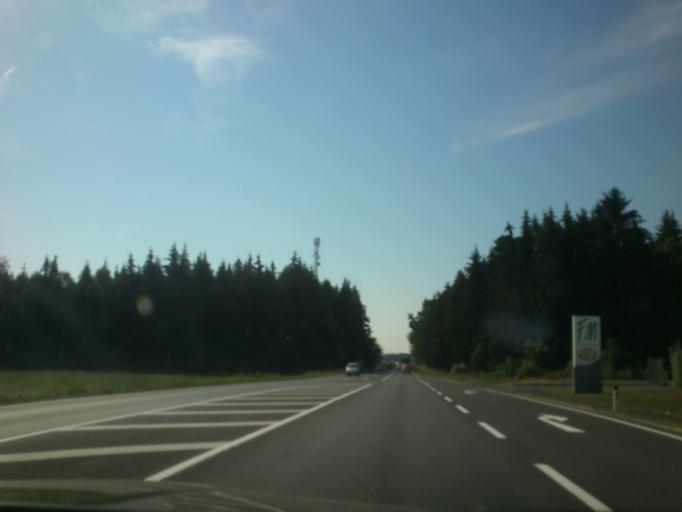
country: AT
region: Upper Austria
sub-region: Politischer Bezirk Freistadt
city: Freistadt
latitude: 48.4798
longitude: 14.4973
